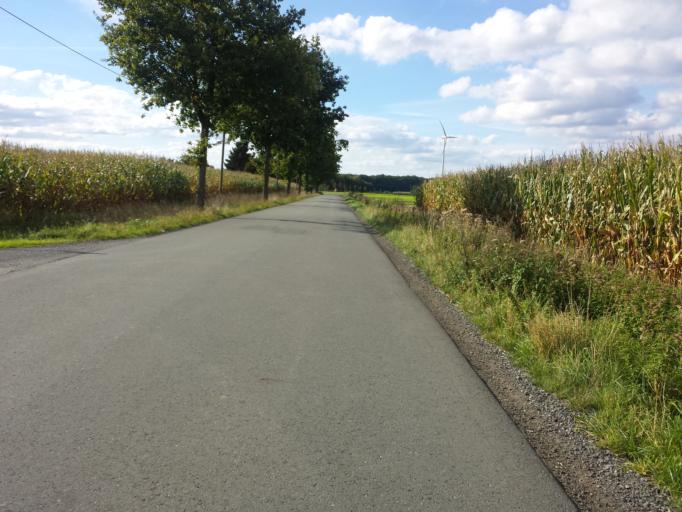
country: DE
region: North Rhine-Westphalia
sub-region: Regierungsbezirk Detmold
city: Langenberg
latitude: 51.7509
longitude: 8.3113
